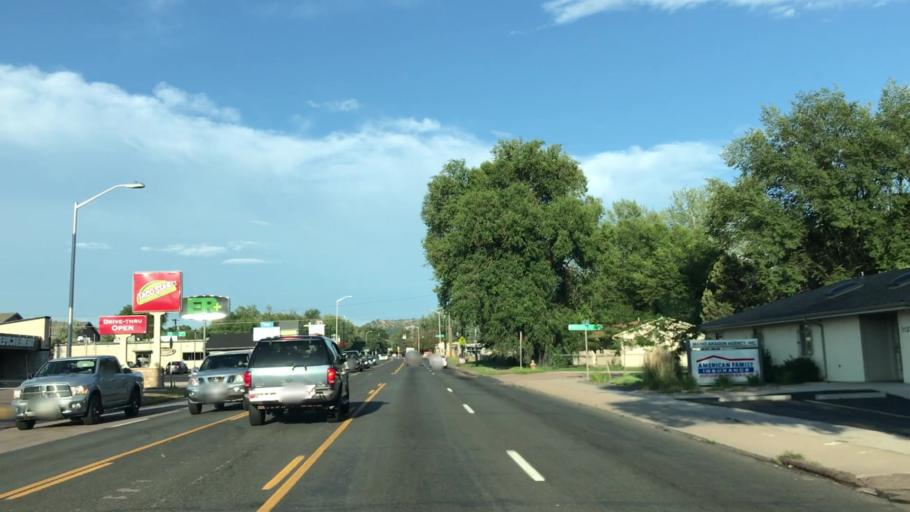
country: US
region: Colorado
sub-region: El Paso County
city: Colorado Springs
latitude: 38.8740
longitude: -104.8062
